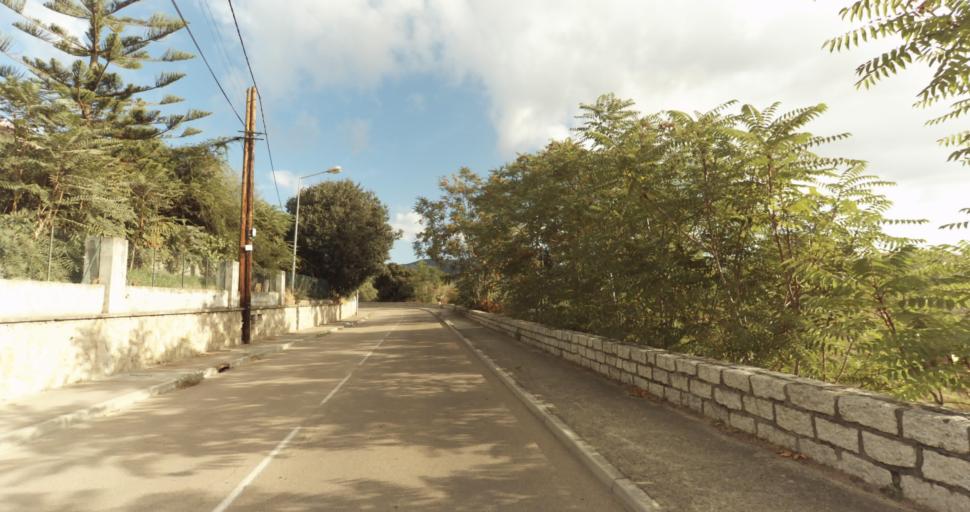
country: FR
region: Corsica
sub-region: Departement de la Corse-du-Sud
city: Ajaccio
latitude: 41.9303
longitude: 8.7263
